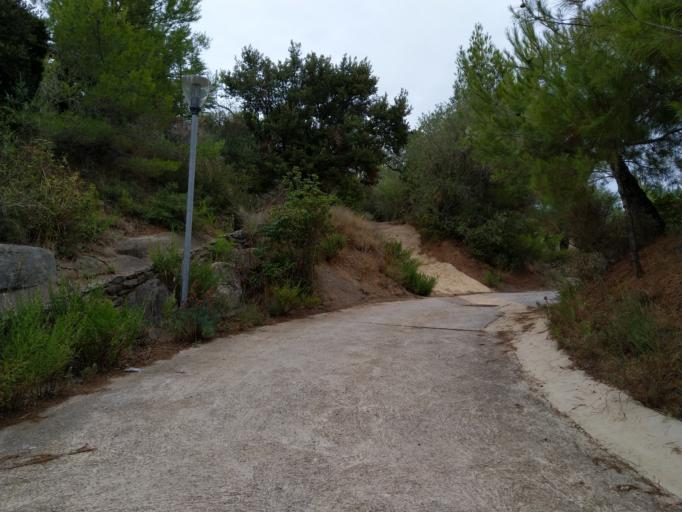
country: FR
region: Languedoc-Roussillon
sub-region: Departement de l'Herault
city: Olonzac
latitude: 43.2983
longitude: 2.7614
